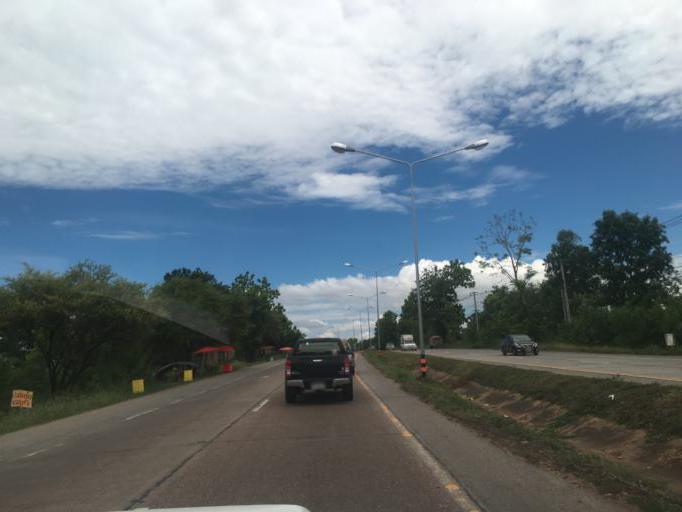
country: TH
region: Khon Kaen
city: Nam Phong
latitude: 16.6522
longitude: 102.8003
